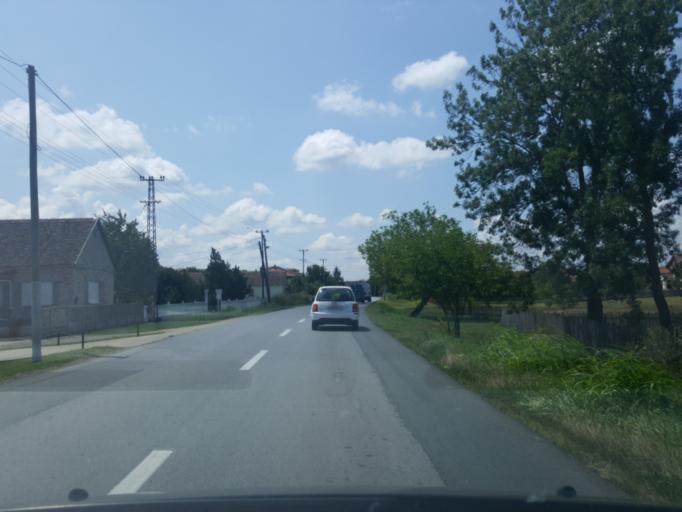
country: RS
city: Salas Nocajski
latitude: 44.9398
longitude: 19.5749
